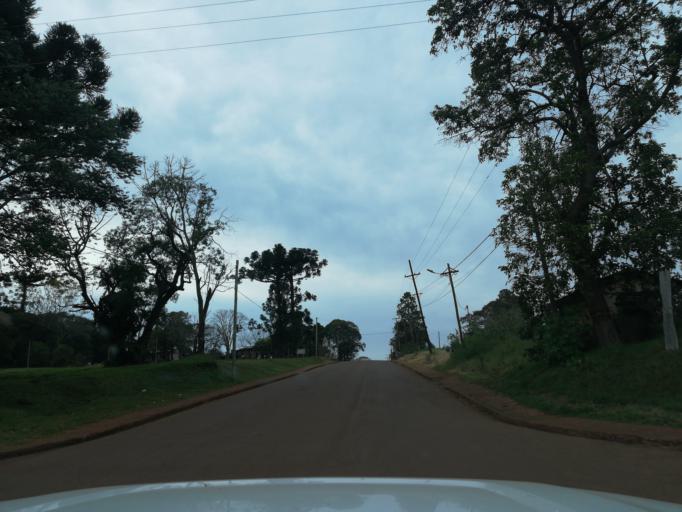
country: AR
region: Misiones
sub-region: Departamento de San Pedro
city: San Pedro
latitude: -26.6235
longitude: -54.1049
